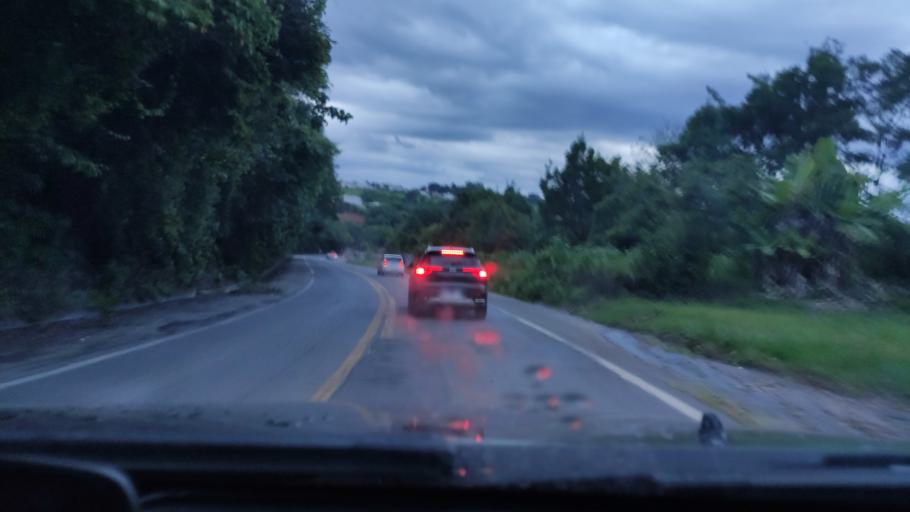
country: BR
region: Sao Paulo
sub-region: Socorro
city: Socorro
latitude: -22.5990
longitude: -46.5186
